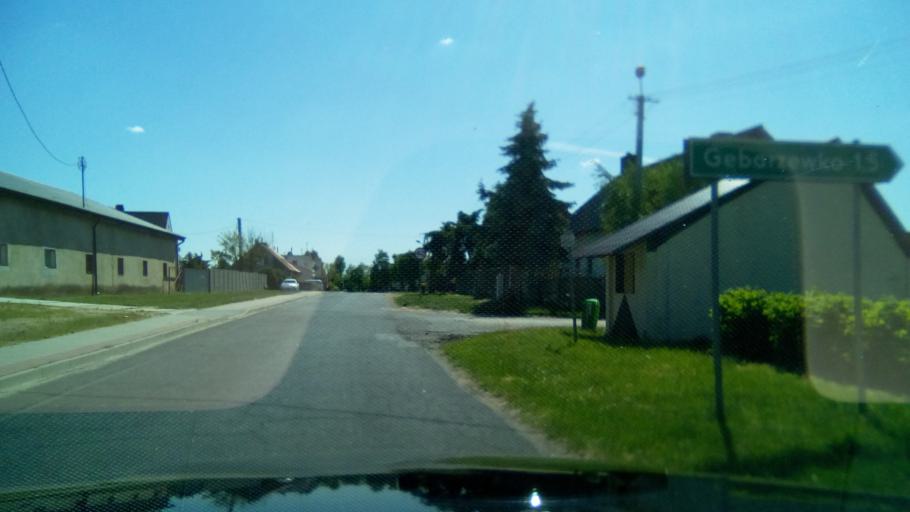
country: PL
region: Greater Poland Voivodeship
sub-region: Powiat gnieznienski
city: Gniezno
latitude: 52.4694
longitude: 17.5611
